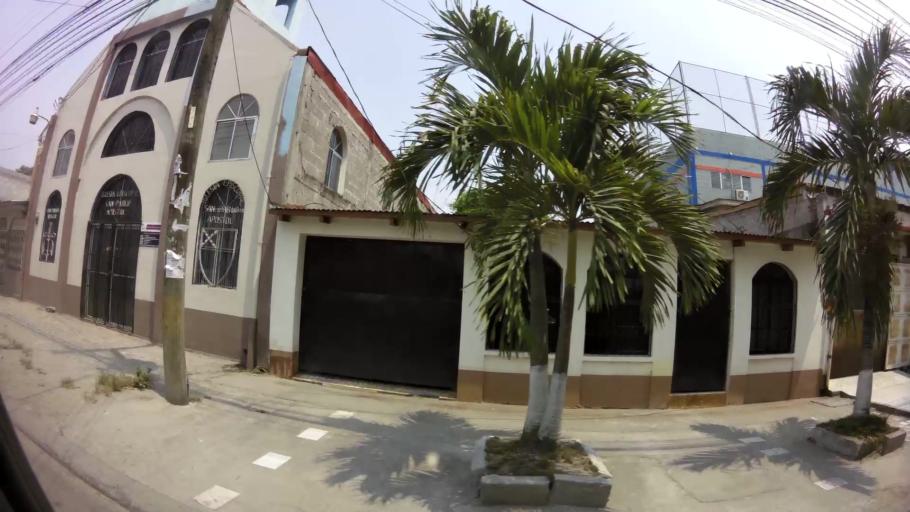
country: HN
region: Cortes
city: San Pedro Sula
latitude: 15.4896
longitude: -87.9866
